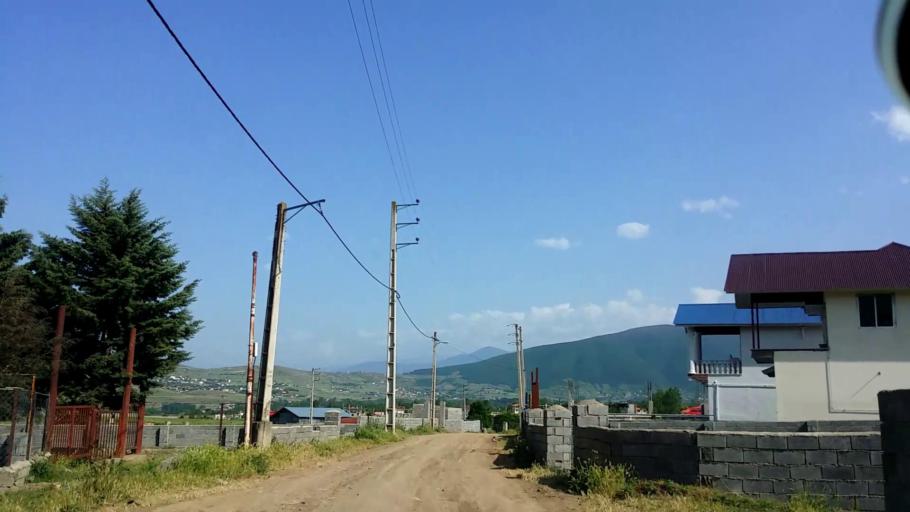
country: IR
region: Mazandaran
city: `Abbasabad
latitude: 36.5447
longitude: 51.1880
